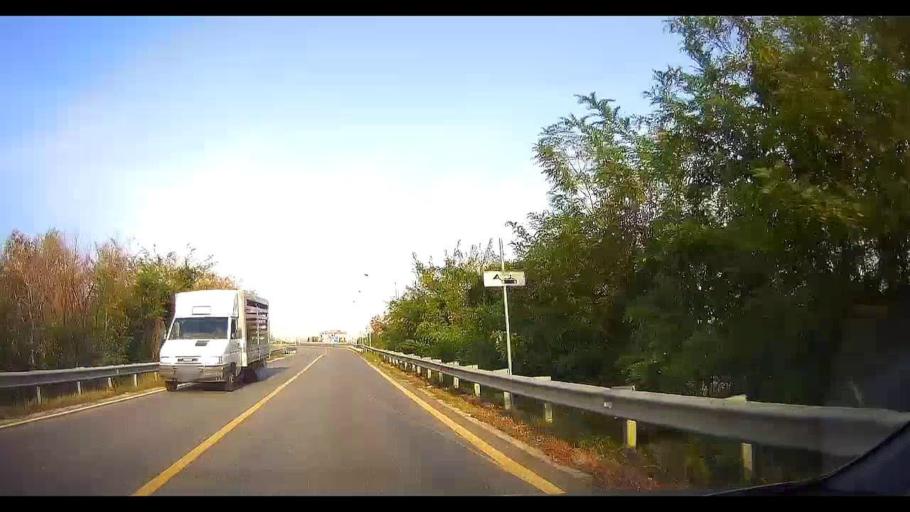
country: IT
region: Calabria
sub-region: Provincia di Cosenza
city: Cariati
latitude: 39.5226
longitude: 16.8986
